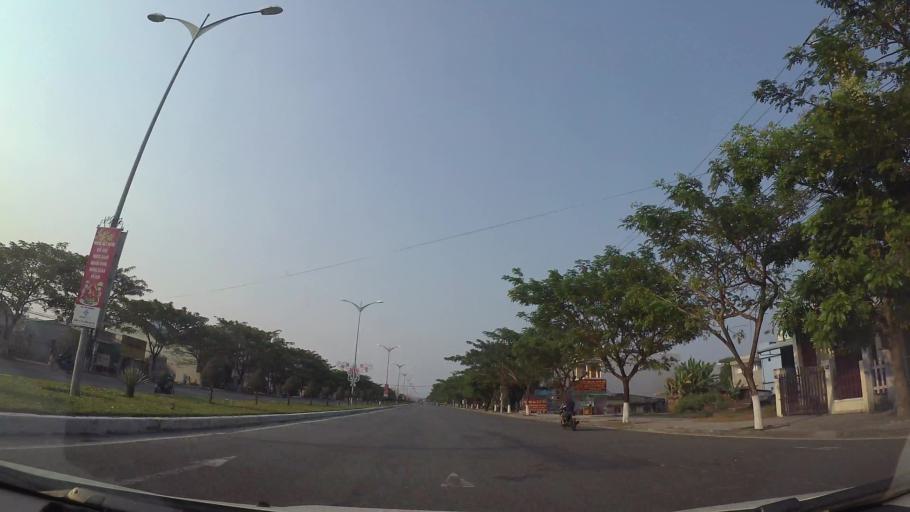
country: VN
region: Da Nang
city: Ngu Hanh Son
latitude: 15.9676
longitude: 108.2548
